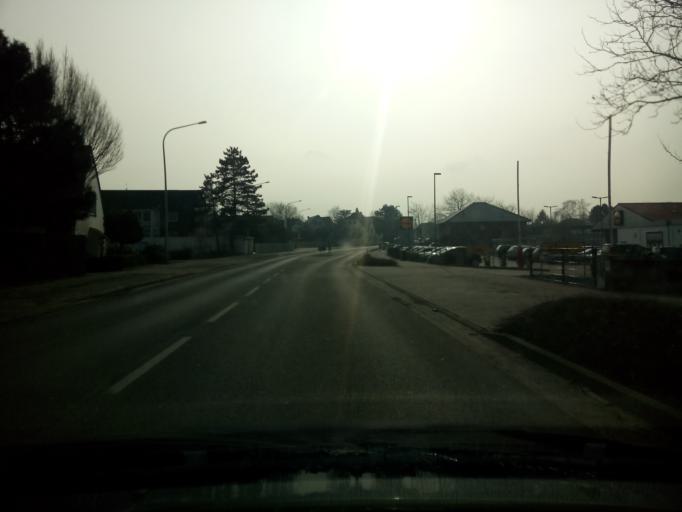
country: DE
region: Lower Saxony
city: Langen
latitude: 53.6108
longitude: 8.5960
